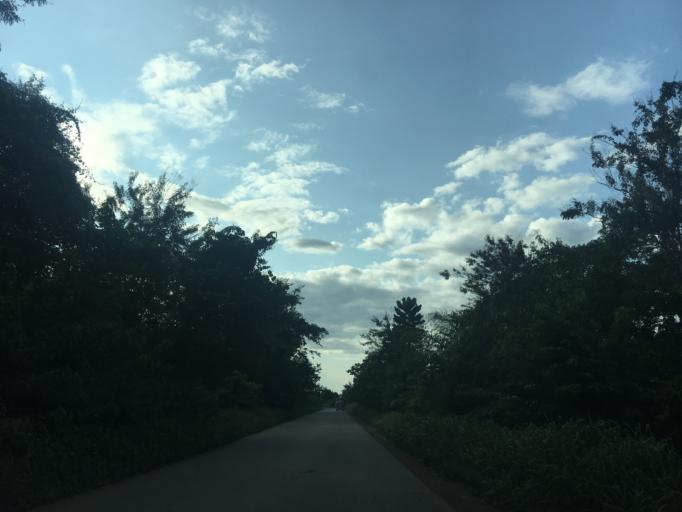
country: GH
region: Western
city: Bibiani
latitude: 6.2813
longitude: -2.2260
